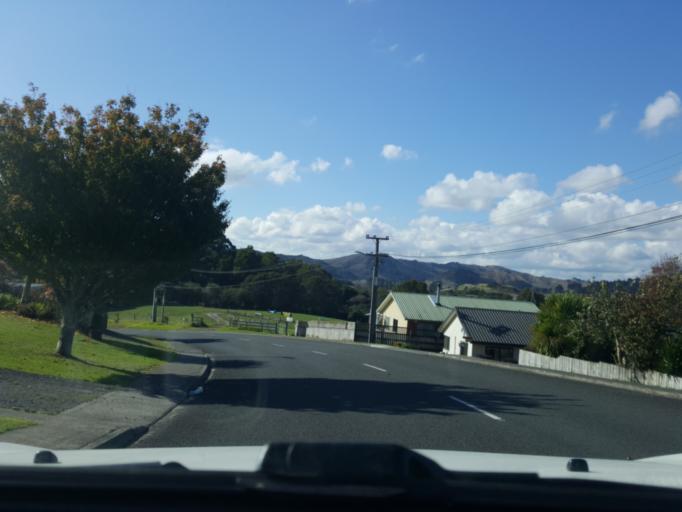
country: NZ
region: Waikato
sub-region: Waikato District
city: Ngaruawahia
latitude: -37.5418
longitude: 175.1731
